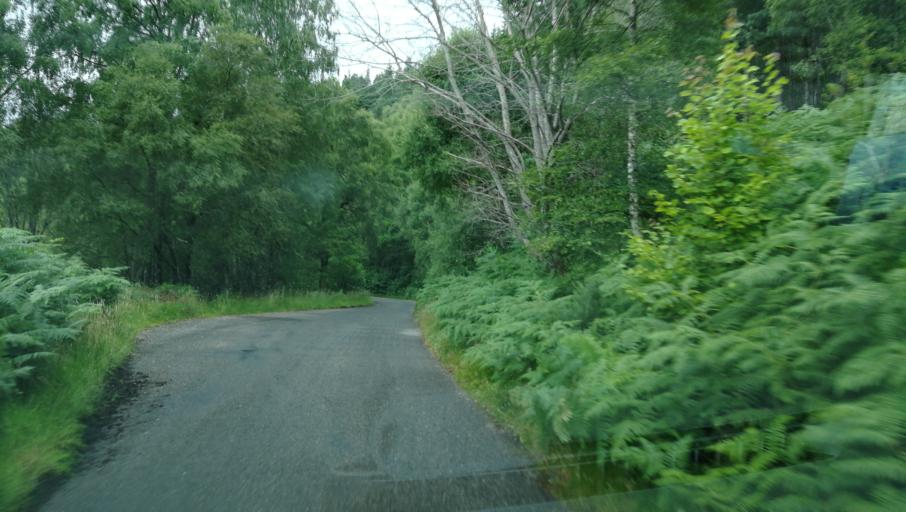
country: GB
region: Scotland
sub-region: Highland
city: Beauly
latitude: 57.3173
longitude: -4.8244
